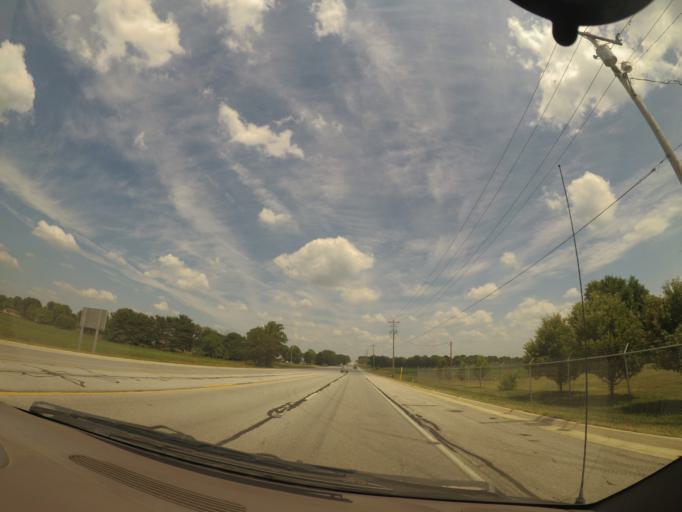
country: US
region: Indiana
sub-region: Elkhart County
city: Dunlap
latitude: 41.6670
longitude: -85.8677
